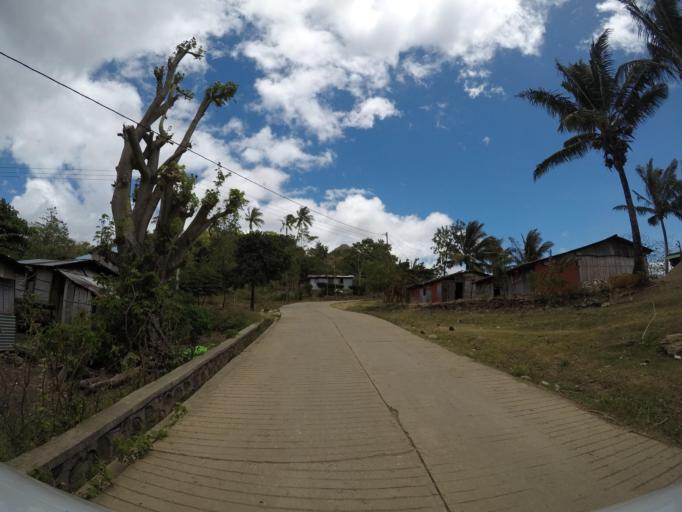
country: TL
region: Lautem
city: Lospalos
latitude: -8.5383
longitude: 126.8267
